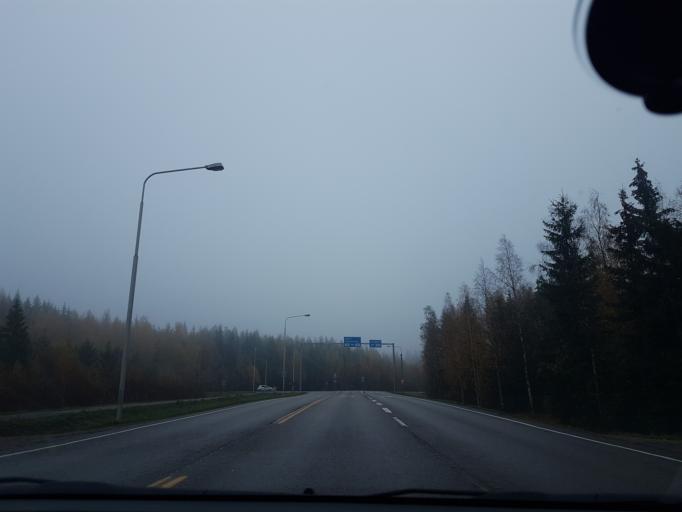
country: FI
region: Uusimaa
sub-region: Helsinki
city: Jaervenpaeae
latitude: 60.4522
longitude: 25.1335
